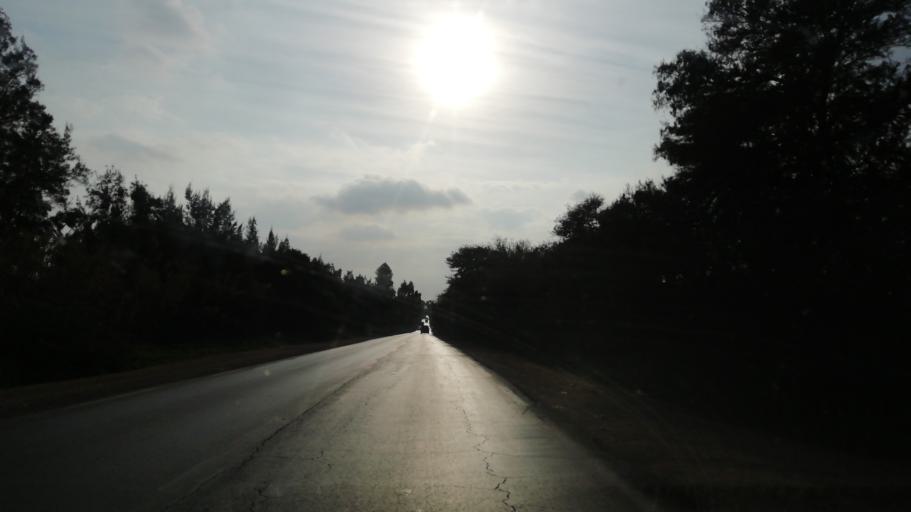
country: DZ
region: Mostaganem
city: Mostaganem
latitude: 35.8350
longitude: 0.0583
